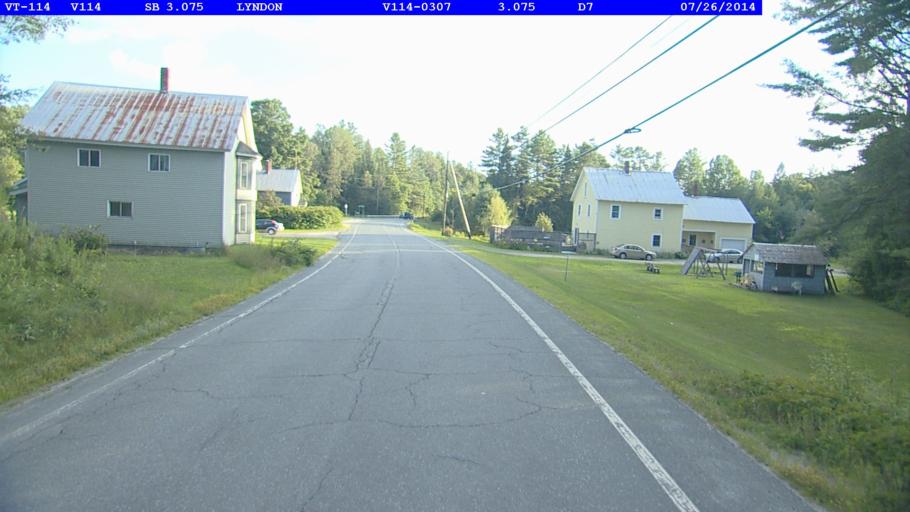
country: US
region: Vermont
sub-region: Caledonia County
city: Lyndonville
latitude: 44.5697
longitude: -71.9533
